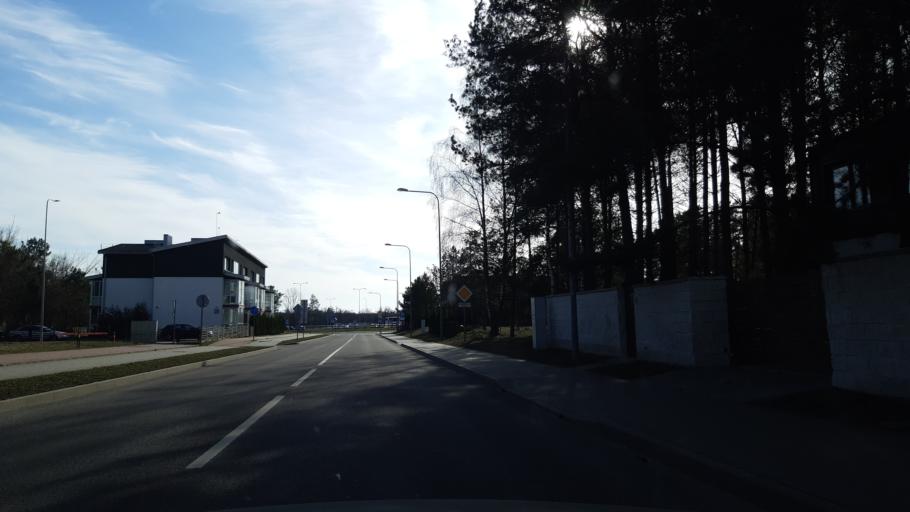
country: LT
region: Alytaus apskritis
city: Druskininkai
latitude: 54.0259
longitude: 23.9813
